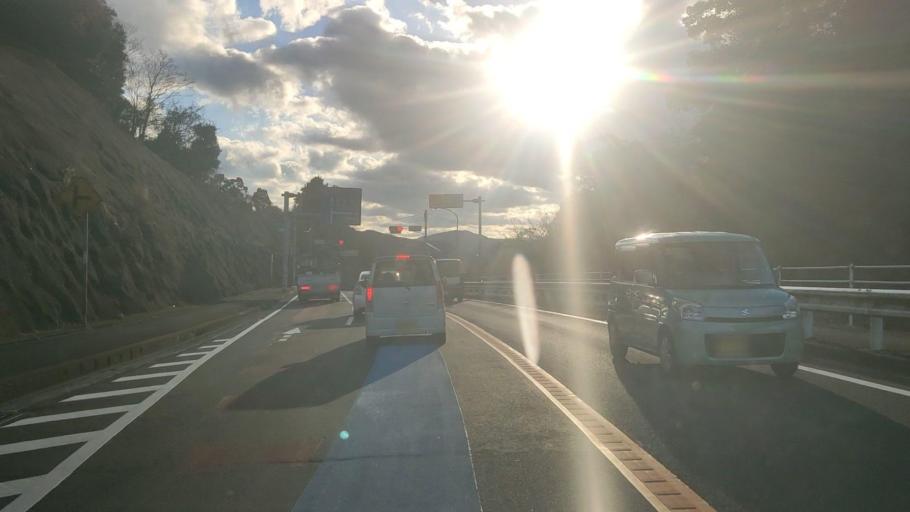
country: JP
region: Saga Prefecture
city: Saga-shi
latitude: 33.2888
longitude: 130.1670
